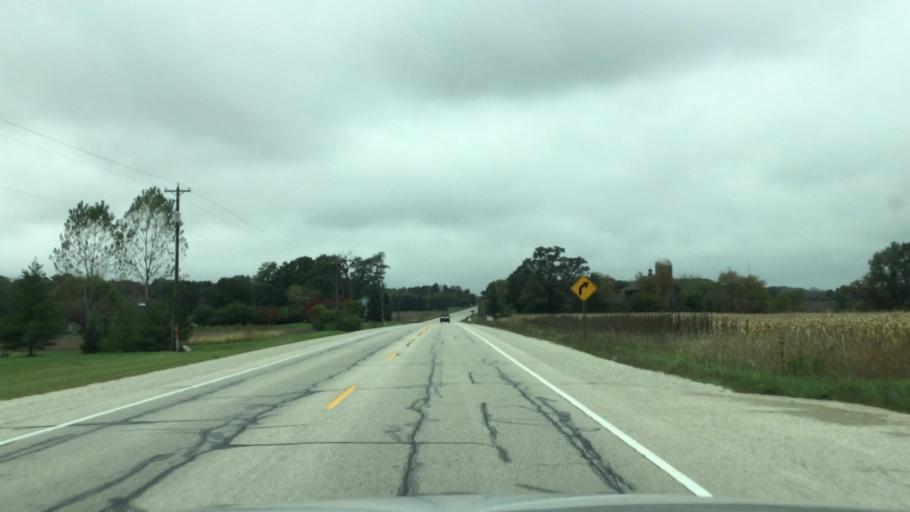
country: US
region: Wisconsin
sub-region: Racine County
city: Eagle Lake
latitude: 42.7413
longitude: -88.1228
